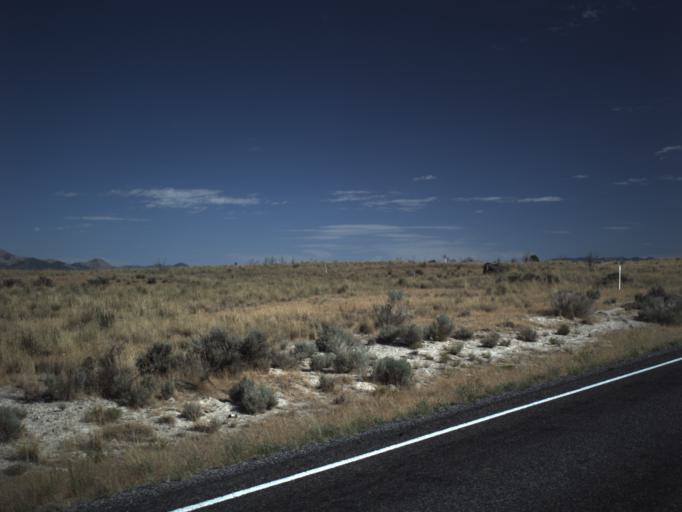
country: US
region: Utah
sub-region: Juab County
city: Mona
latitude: 39.7329
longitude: -112.1926
